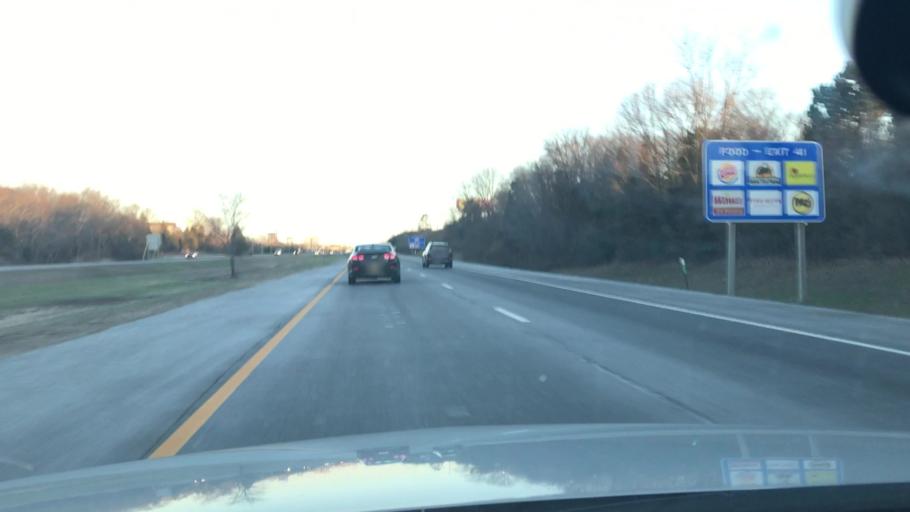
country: US
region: New Jersey
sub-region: Gloucester County
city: Turnersville
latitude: 39.7407
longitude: -75.0162
